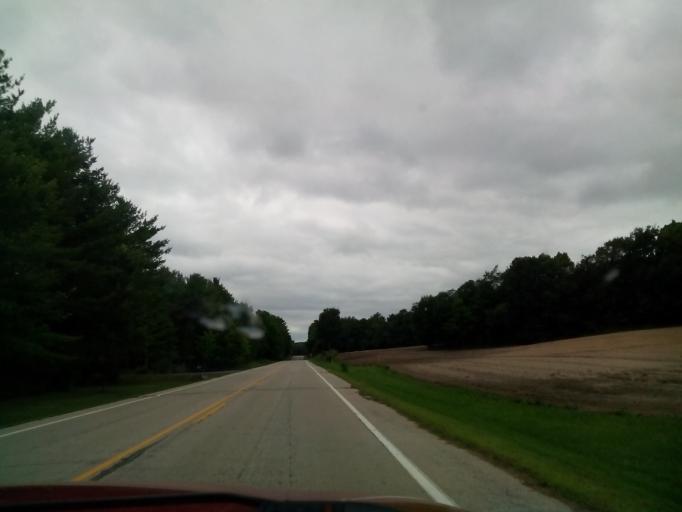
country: US
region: Wisconsin
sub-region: Outagamie County
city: Hortonville
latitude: 44.3557
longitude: -88.5978
